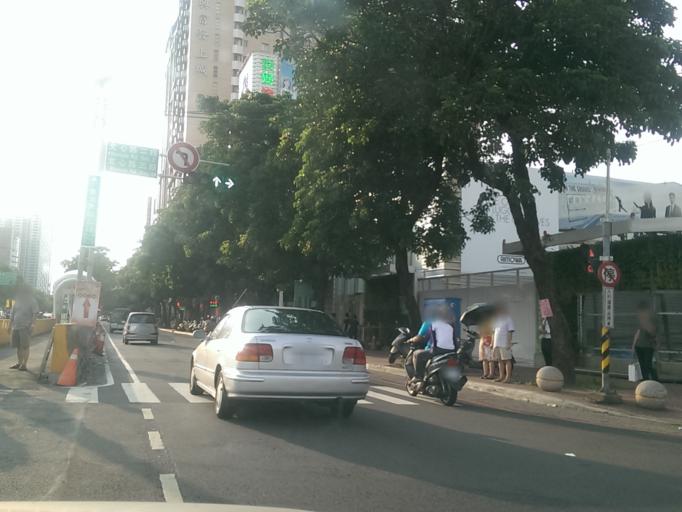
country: TW
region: Taiwan
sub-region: Taichung City
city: Taichung
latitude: 24.1629
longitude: 120.6496
